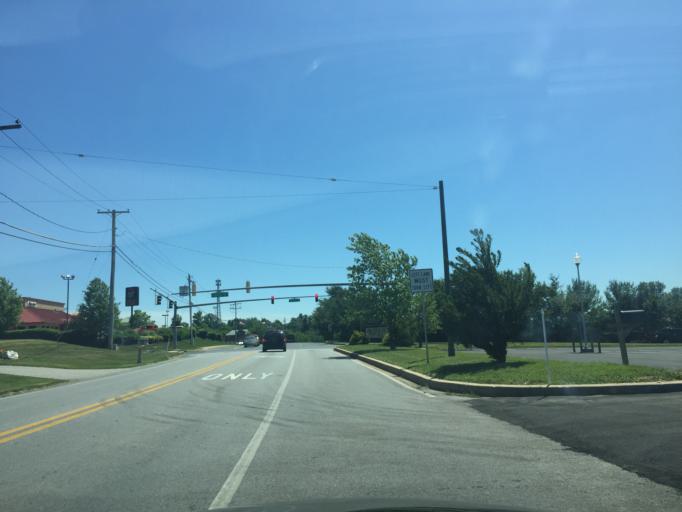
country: US
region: Maryland
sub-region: Carroll County
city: Westminster
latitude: 39.5761
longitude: -76.9798
